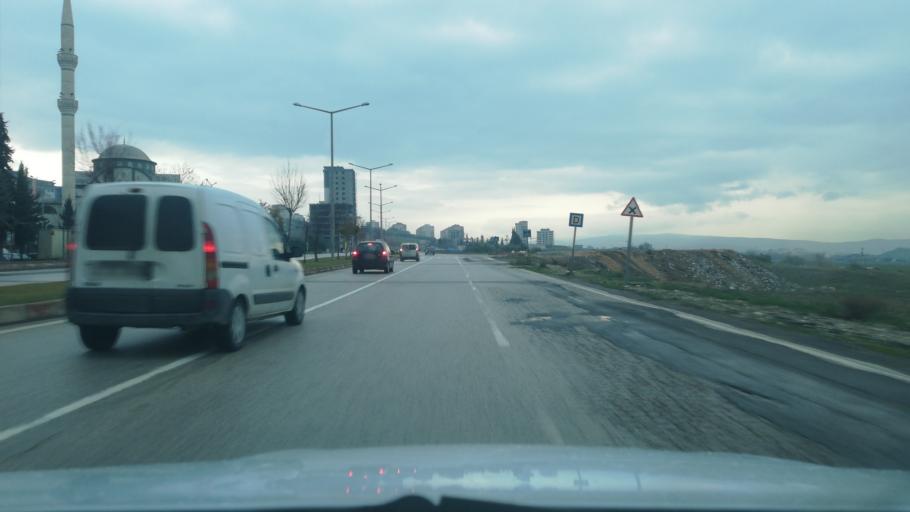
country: TR
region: Kahramanmaras
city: Kahramanmaras
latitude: 37.5825
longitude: 36.9852
